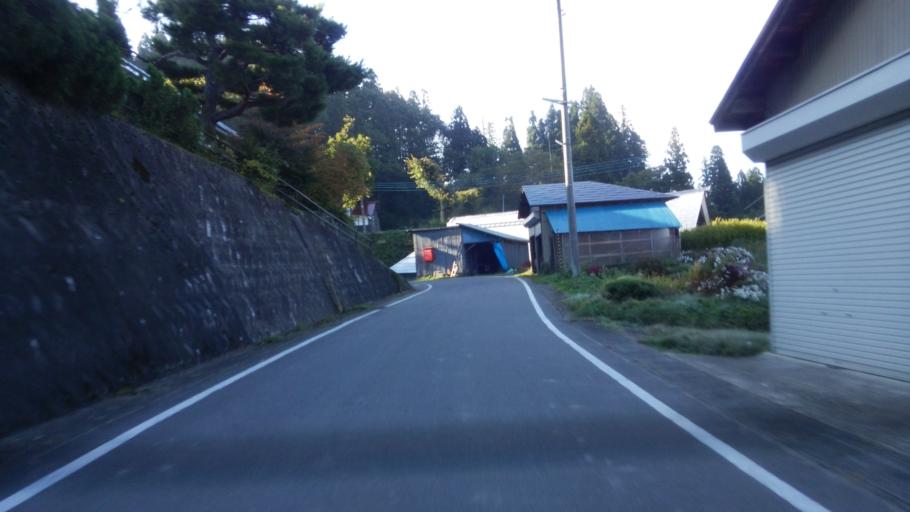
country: JP
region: Fukushima
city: Kitakata
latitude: 37.4584
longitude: 139.7234
